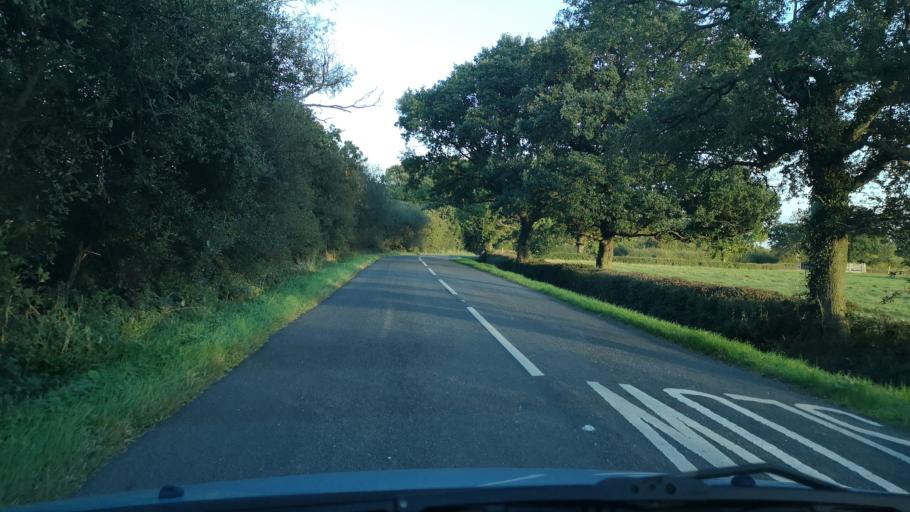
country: GB
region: England
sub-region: Doncaster
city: Fenwick
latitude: 53.6311
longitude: -1.0696
